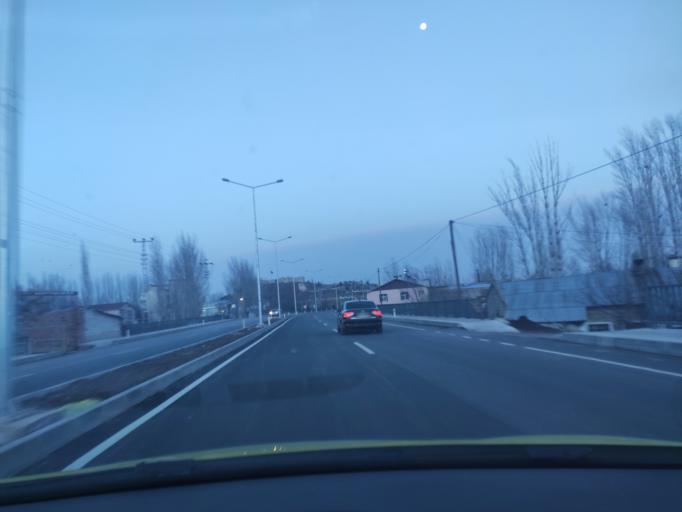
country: TR
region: Bayburt
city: Aydintepe
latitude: 40.3884
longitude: 40.1428
